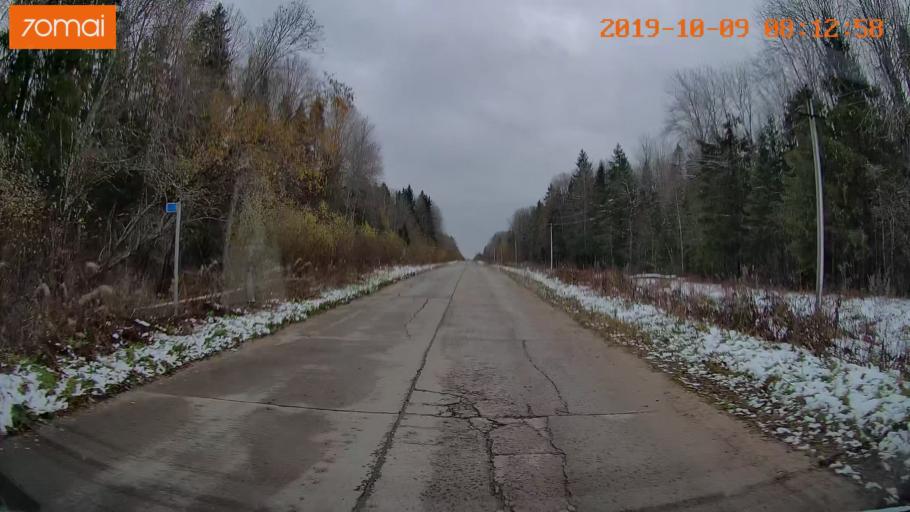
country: RU
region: Vologda
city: Gryazovets
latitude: 58.7212
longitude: 40.1328
